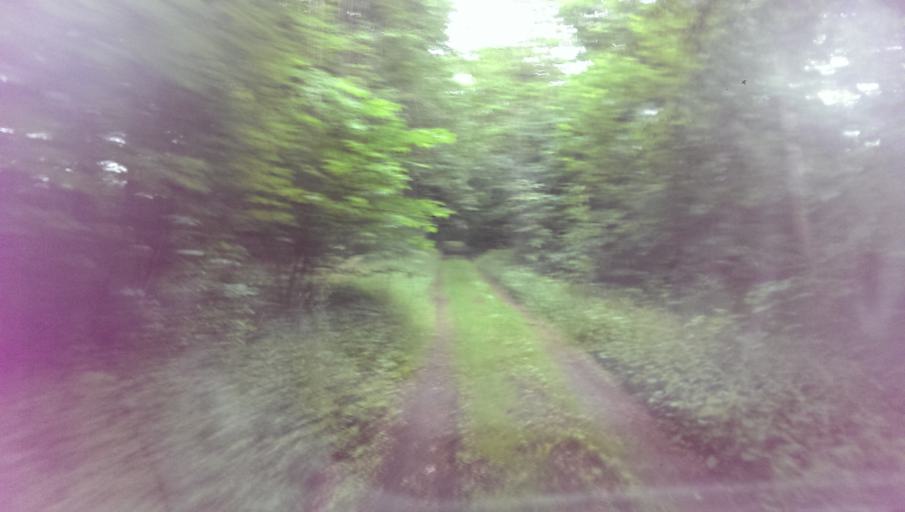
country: DK
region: South Denmark
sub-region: Esbjerg Kommune
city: Bramming
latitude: 55.4424
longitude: 8.7165
